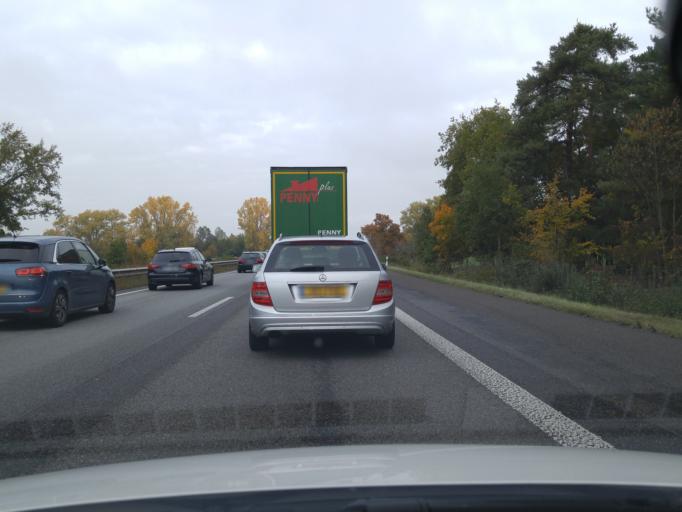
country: DE
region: Rheinland-Pfalz
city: Schifferstadt
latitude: 49.3748
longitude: 8.3436
